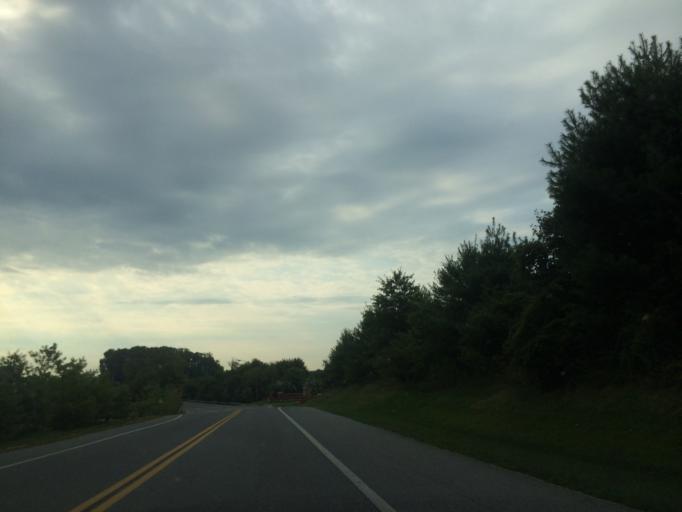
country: US
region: Maryland
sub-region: Howard County
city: Fulton
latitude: 39.1635
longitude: -76.9065
